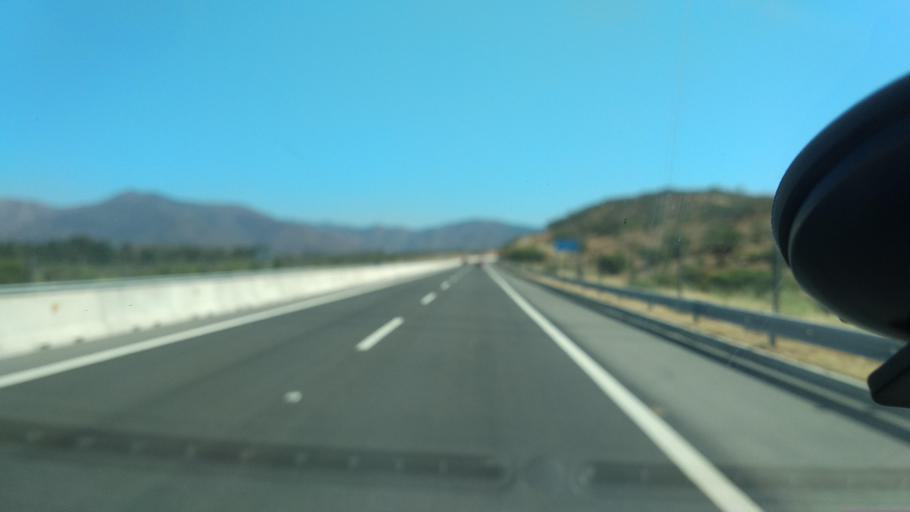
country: CL
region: Valparaiso
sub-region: Provincia de Marga Marga
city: Limache
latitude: -33.0218
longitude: -71.3194
